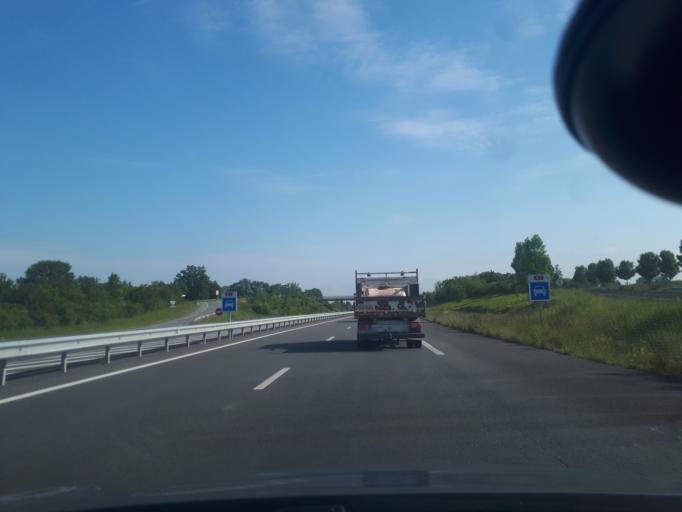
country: FR
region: Rhone-Alpes
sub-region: Departement de la Loire
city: Ambierle
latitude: 46.1385
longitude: 3.8996
